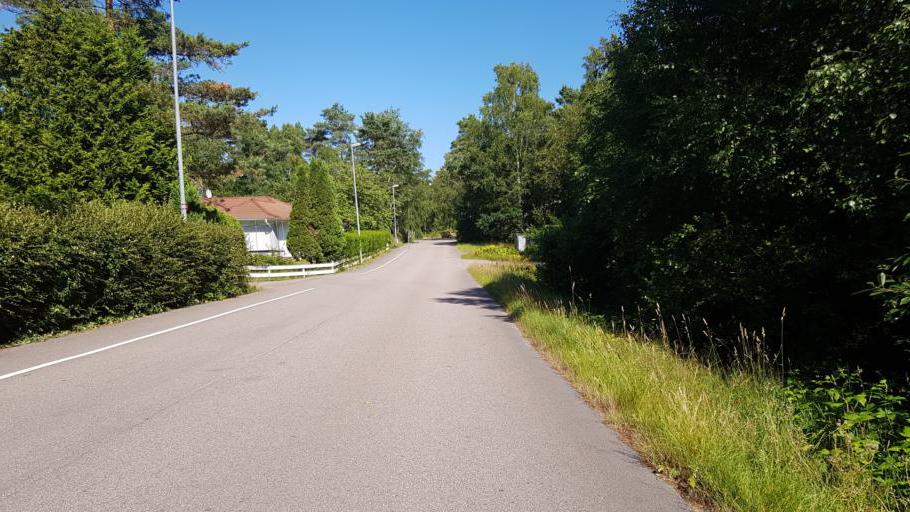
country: SE
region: Vaestra Goetaland
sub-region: Partille Kommun
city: Furulund
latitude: 57.6957
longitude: 12.1418
